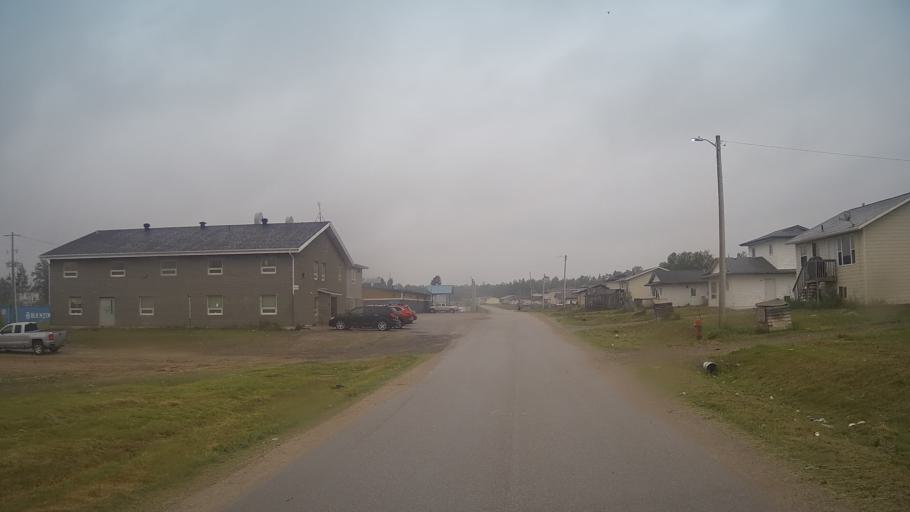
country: CA
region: Ontario
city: Greenstone
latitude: 49.7872
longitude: -86.5697
